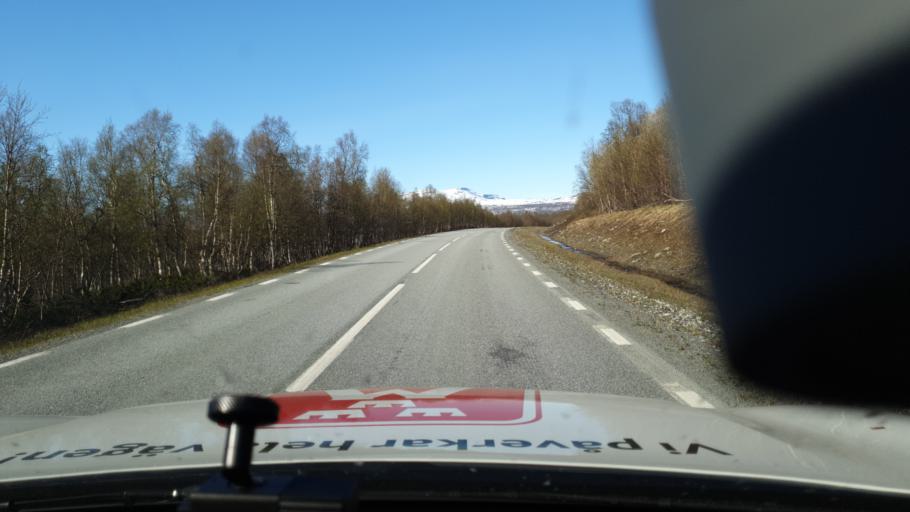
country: NO
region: Nordland
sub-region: Rana
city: Mo i Rana
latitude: 65.9876
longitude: 15.0678
